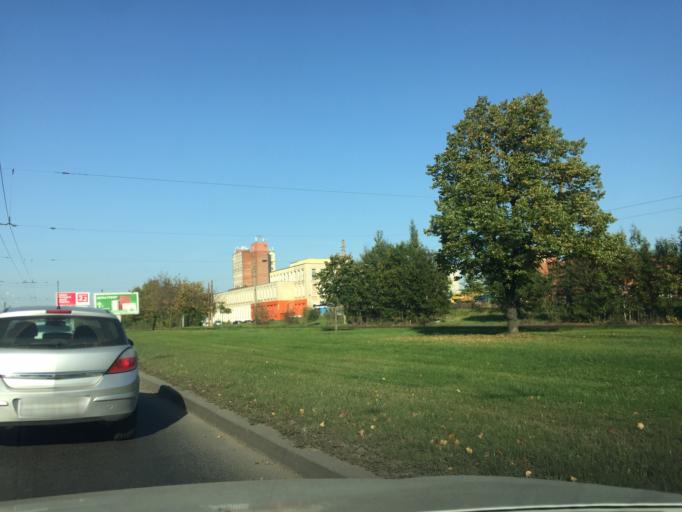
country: RU
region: Leningrad
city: Akademicheskoe
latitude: 59.9999
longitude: 30.4373
